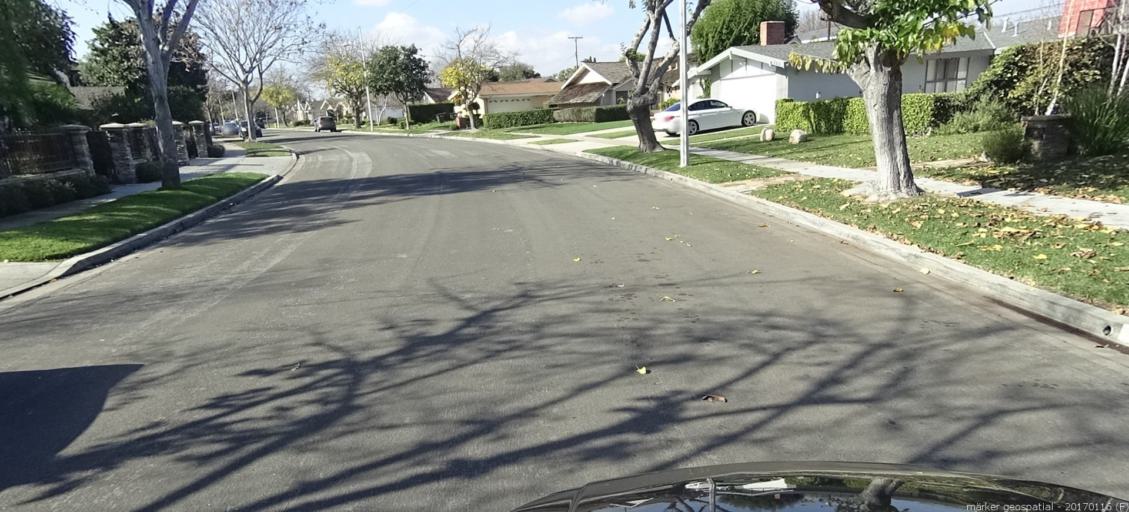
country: US
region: California
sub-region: Orange County
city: Rossmoor
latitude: 33.7817
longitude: -118.0767
